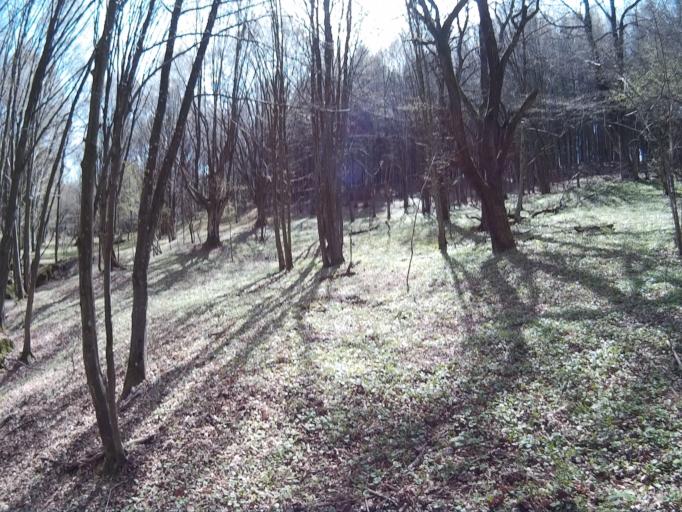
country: HU
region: Veszprem
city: Herend
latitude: 47.2074
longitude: 17.7737
